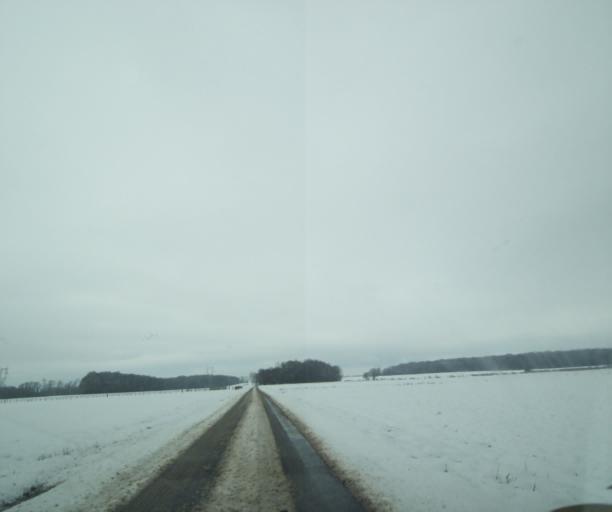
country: FR
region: Champagne-Ardenne
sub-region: Departement de la Haute-Marne
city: Montier-en-Der
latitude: 48.5117
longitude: 4.7573
